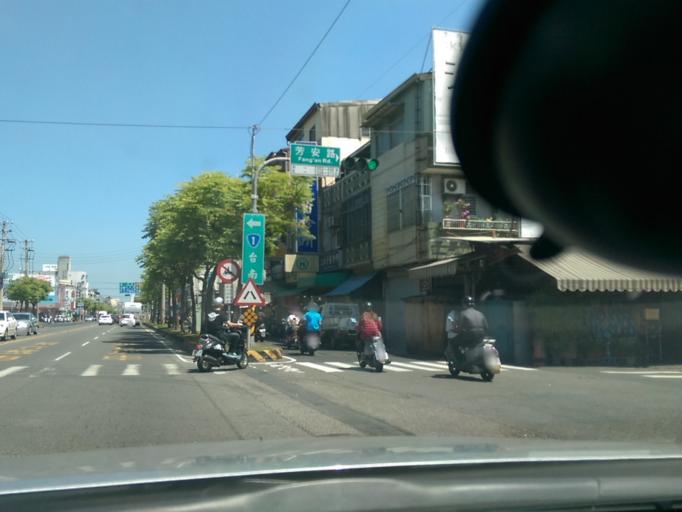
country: TW
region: Taiwan
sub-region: Chiayi
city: Jiayi Shi
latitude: 23.4679
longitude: 120.4545
